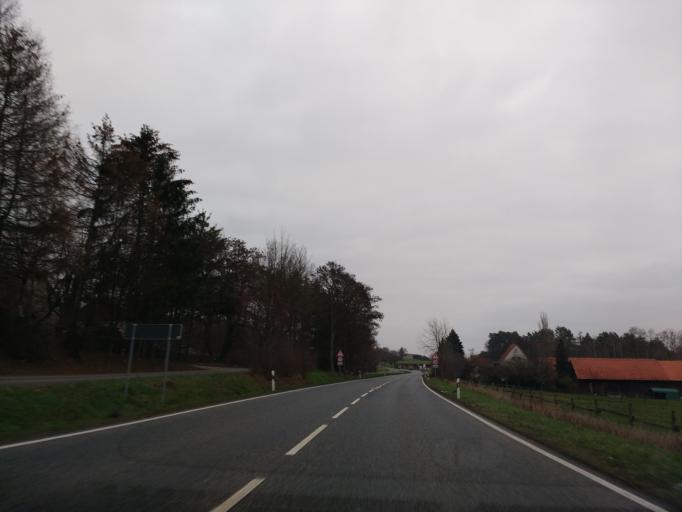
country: DE
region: Hesse
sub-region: Regierungsbezirk Kassel
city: Alheim
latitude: 51.0625
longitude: 9.6242
